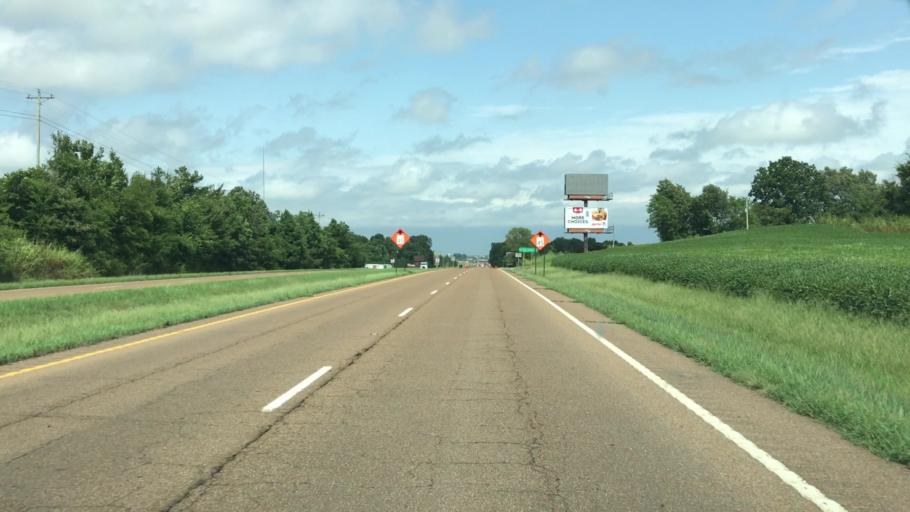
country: US
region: Tennessee
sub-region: Obion County
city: Englewood
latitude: 36.3818
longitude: -89.1107
